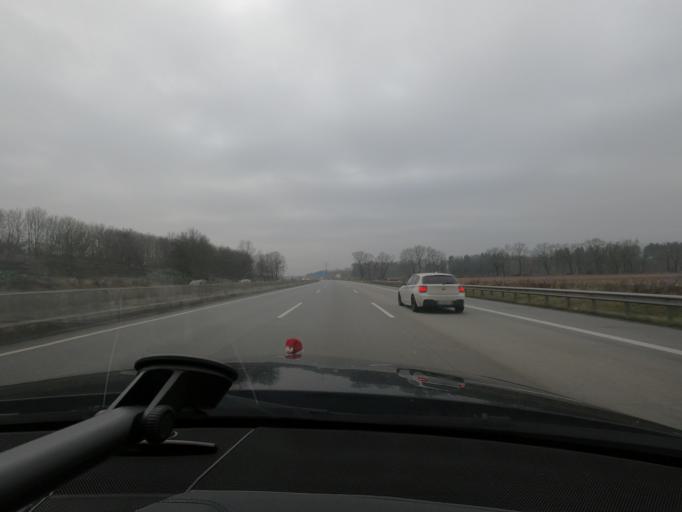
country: DE
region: Schleswig-Holstein
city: Bonningstedt
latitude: 53.6583
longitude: 9.9324
